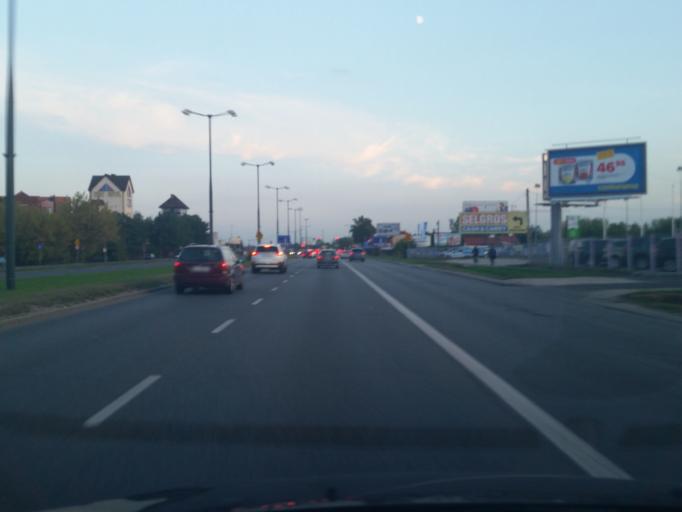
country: PL
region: Masovian Voivodeship
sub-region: Warszawa
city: Bialoleka
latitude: 52.3461
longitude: 20.9494
